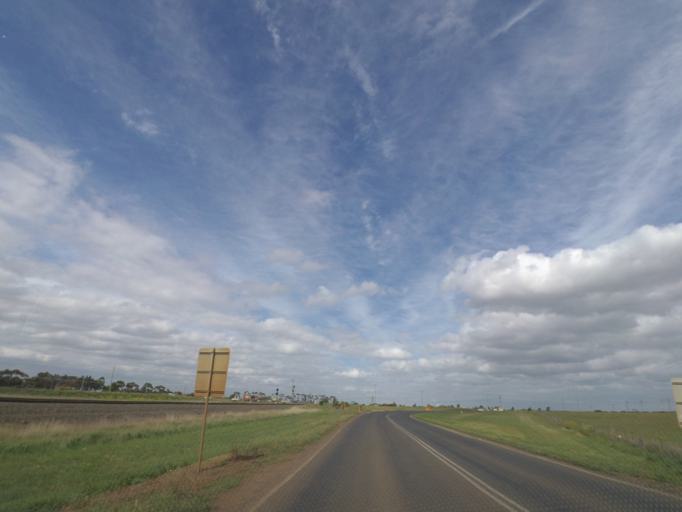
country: AU
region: Victoria
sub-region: Melton
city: Rockbank
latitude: -37.7512
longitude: 144.7006
